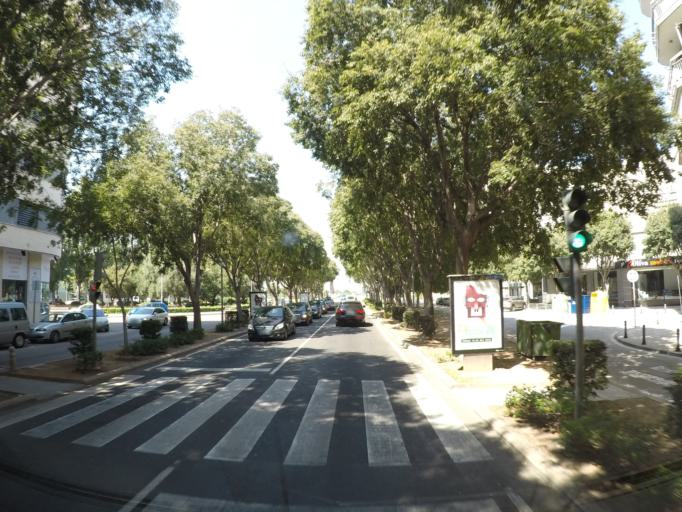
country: ES
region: Valencia
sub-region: Provincia de Valencia
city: Oliva
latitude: 38.9234
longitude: -0.1248
